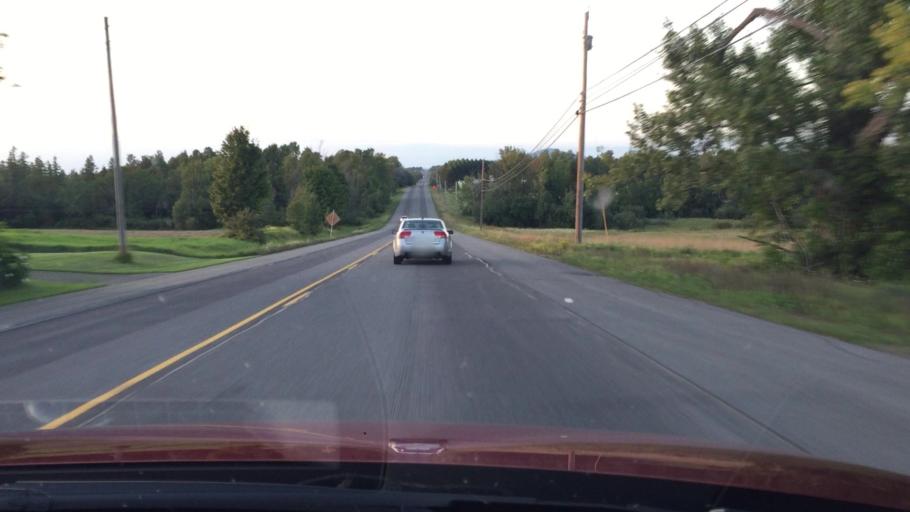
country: US
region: Maine
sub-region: Aroostook County
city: Houlton
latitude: 46.3545
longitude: -67.8422
